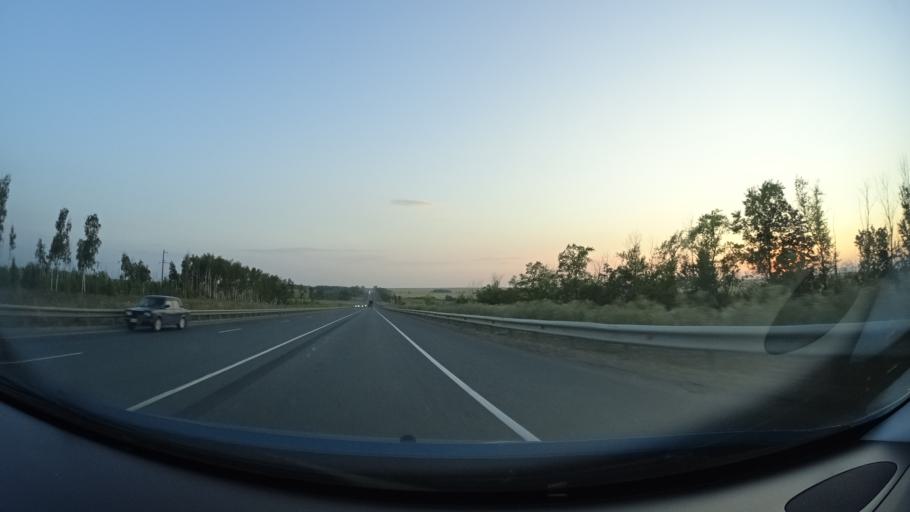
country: RU
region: Samara
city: Sukhodol
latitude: 53.8472
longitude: 51.1325
